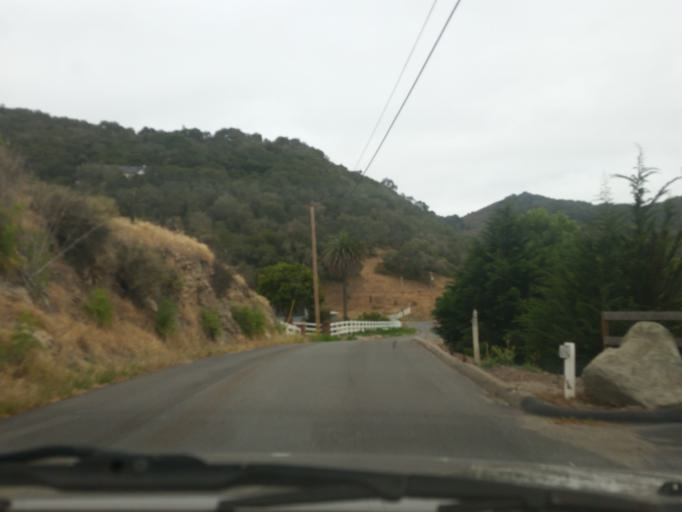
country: US
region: California
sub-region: San Luis Obispo County
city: Avila Beach
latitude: 35.1860
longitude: -120.6972
